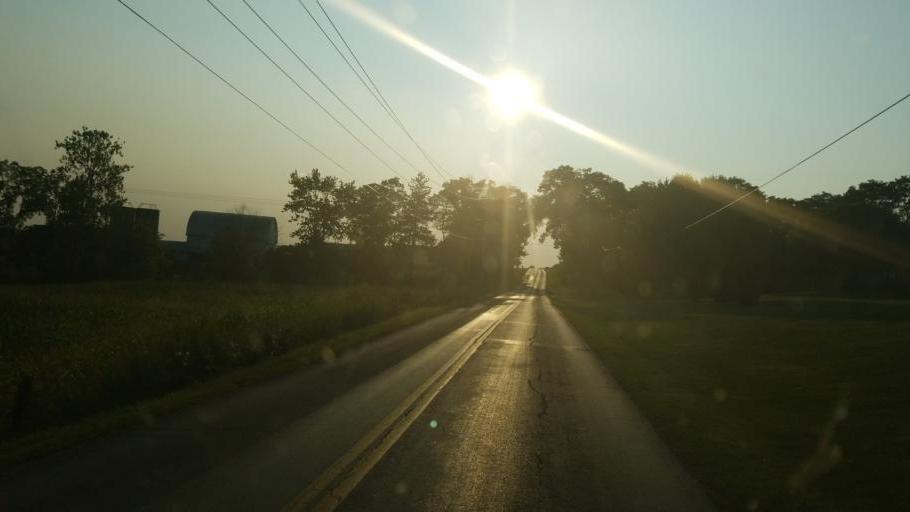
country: US
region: Ohio
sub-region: Wayne County
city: Shreve
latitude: 40.6709
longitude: -81.9308
